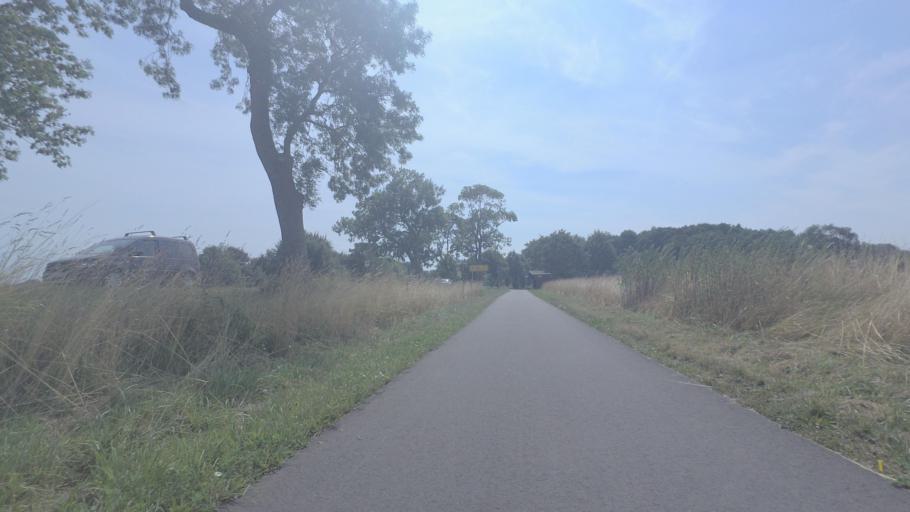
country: DE
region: Mecklenburg-Vorpommern
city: Garz
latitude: 54.2539
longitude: 13.3491
